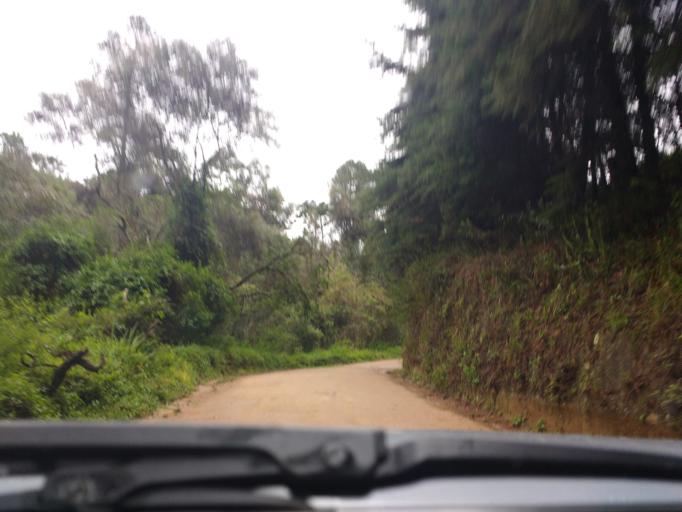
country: BR
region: Minas Gerais
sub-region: Cambui
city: Cambui
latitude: -22.7445
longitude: -45.9163
